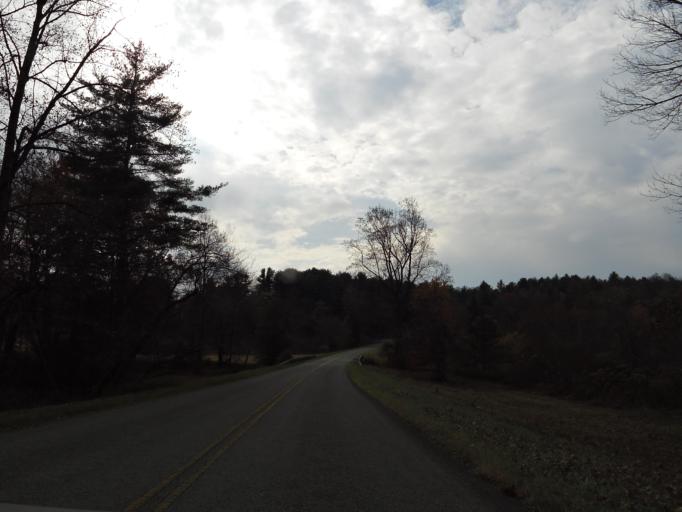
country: US
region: Virginia
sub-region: City of Galax
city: Galax
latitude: 36.5707
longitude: -80.8582
